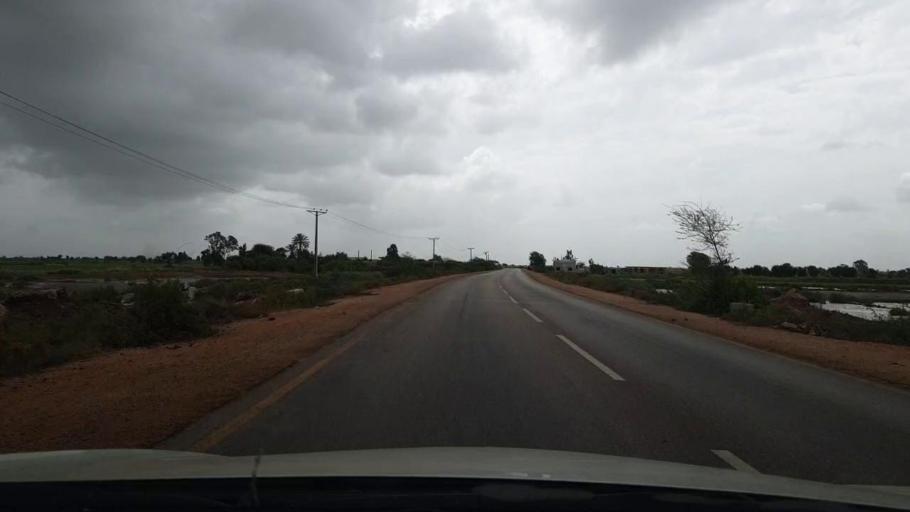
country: PK
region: Sindh
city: Mirpur Batoro
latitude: 24.5983
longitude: 68.2197
